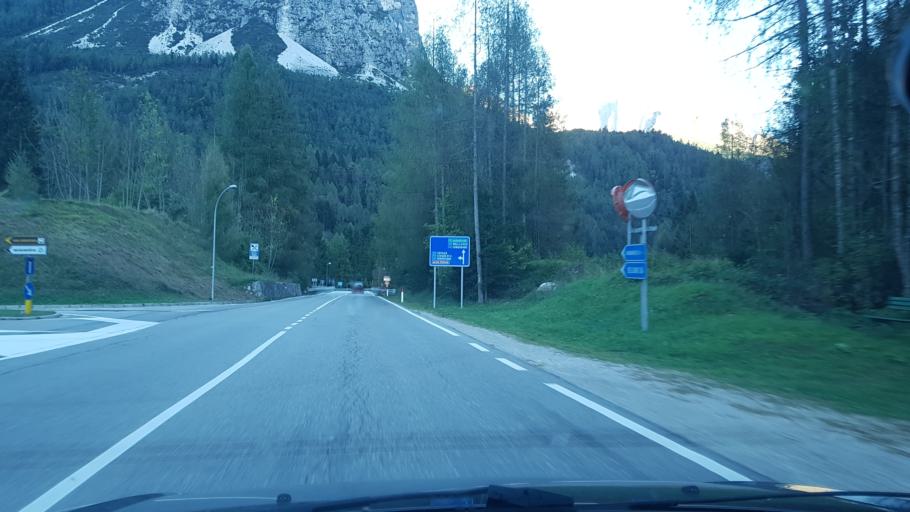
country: IT
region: Veneto
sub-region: Provincia di Belluno
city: Forno di Zoldo
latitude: 46.3456
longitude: 12.1900
